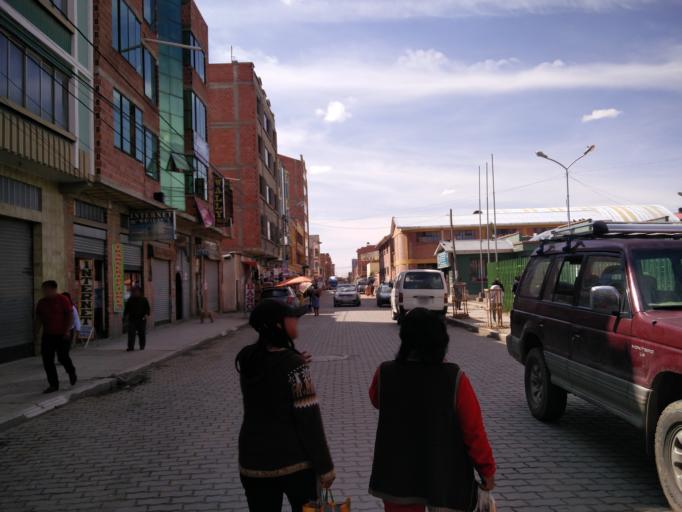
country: BO
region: La Paz
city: La Paz
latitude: -16.5320
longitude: -68.1924
